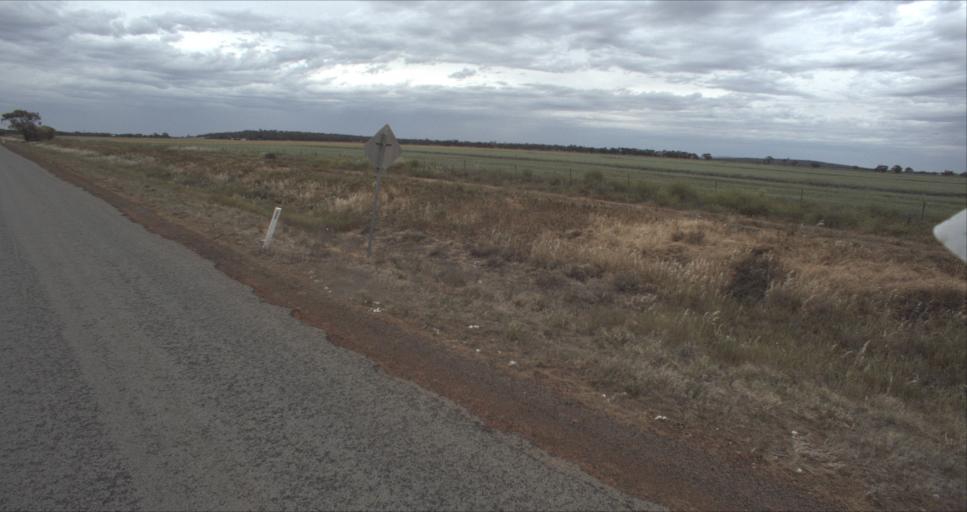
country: AU
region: New South Wales
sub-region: Leeton
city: Leeton
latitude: -34.4350
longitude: 146.3343
